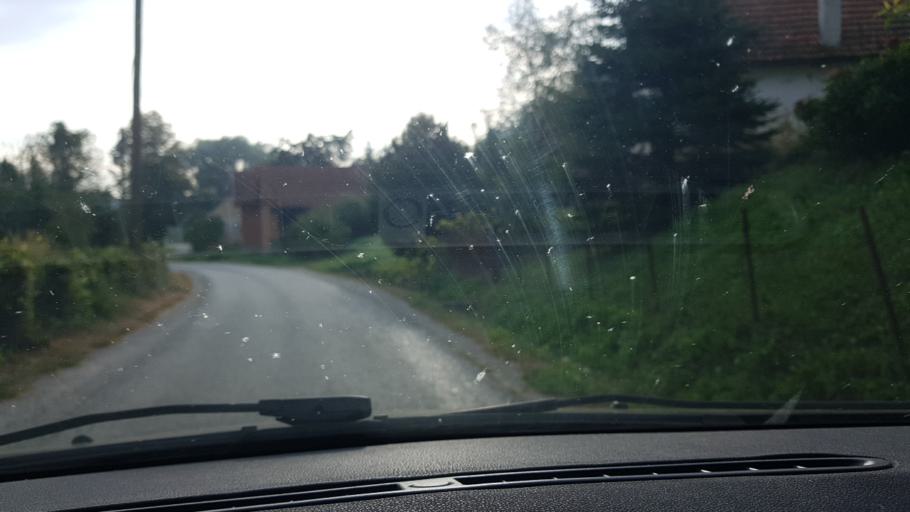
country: HR
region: Krapinsko-Zagorska
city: Zlatar
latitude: 46.1009
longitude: 16.1198
